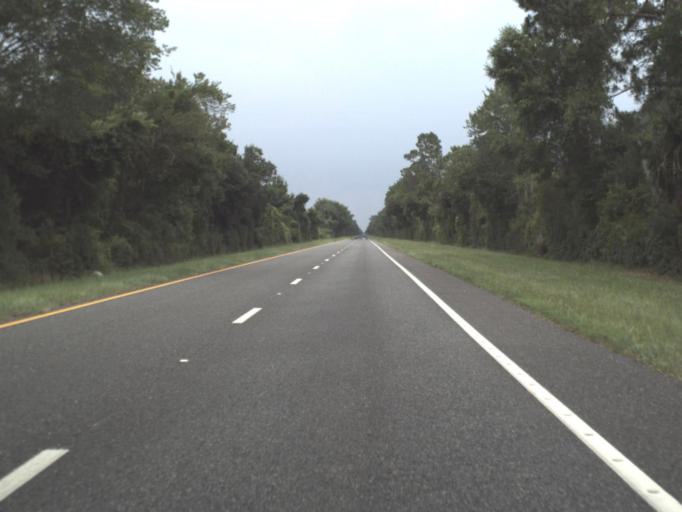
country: US
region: Florida
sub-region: Levy County
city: Bronson
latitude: 29.3089
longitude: -82.7574
